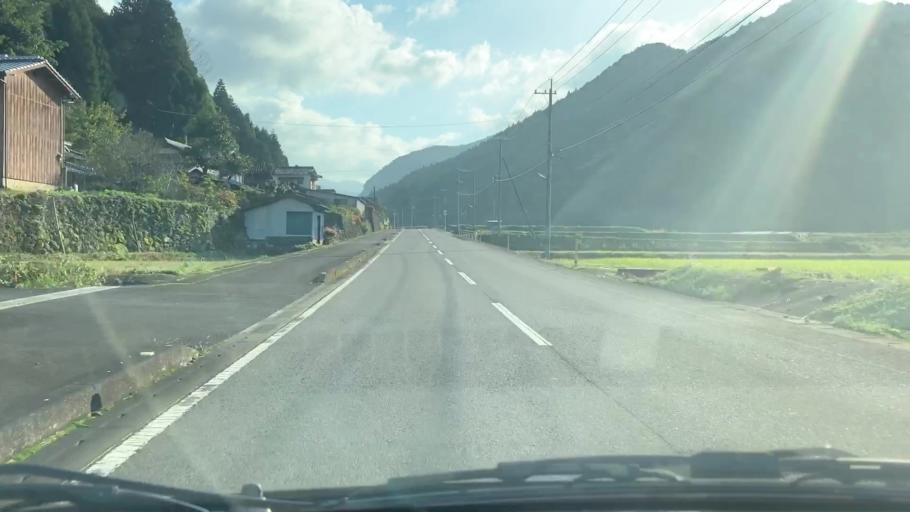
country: JP
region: Saga Prefecture
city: Kashima
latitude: 33.0623
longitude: 130.0702
